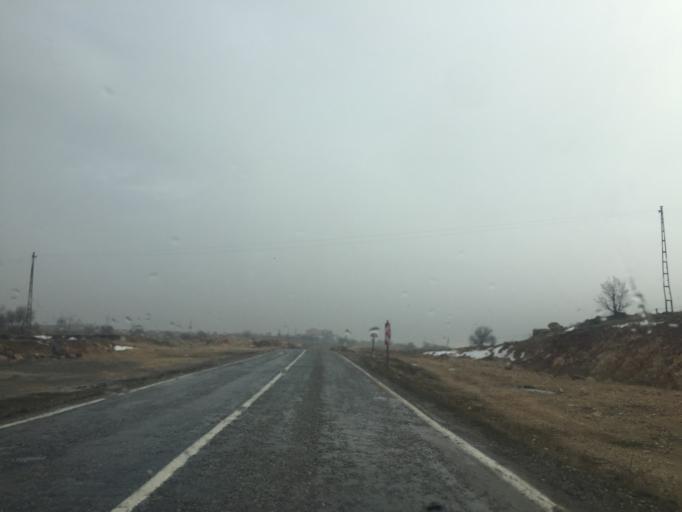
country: TR
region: Mardin
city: Omerli
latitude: 37.3952
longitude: 40.9226
